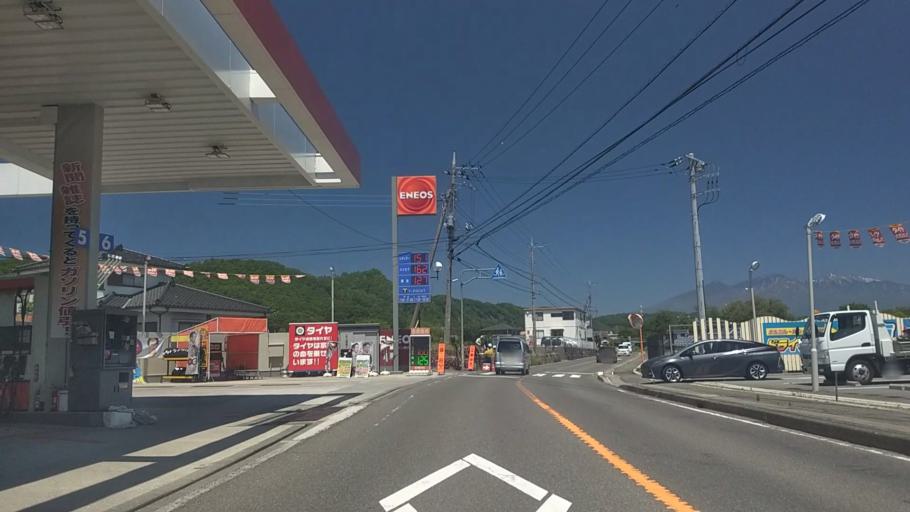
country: JP
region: Yamanashi
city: Nirasaki
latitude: 35.7624
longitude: 138.4292
